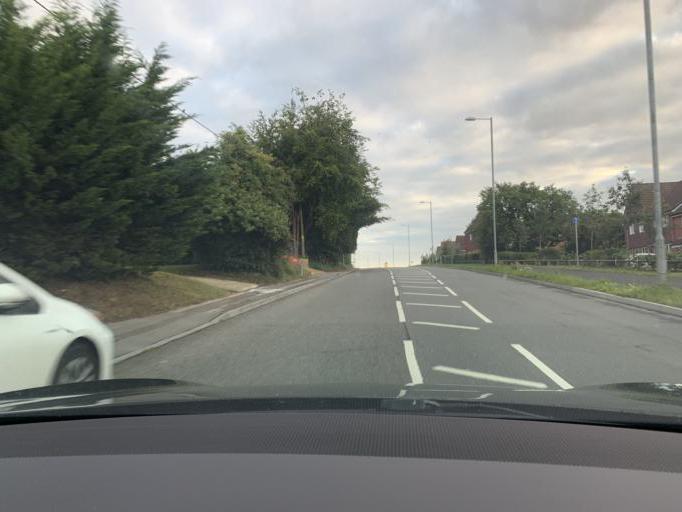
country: GB
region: England
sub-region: Wiltshire
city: Tidworth
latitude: 51.2447
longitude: -1.6653
